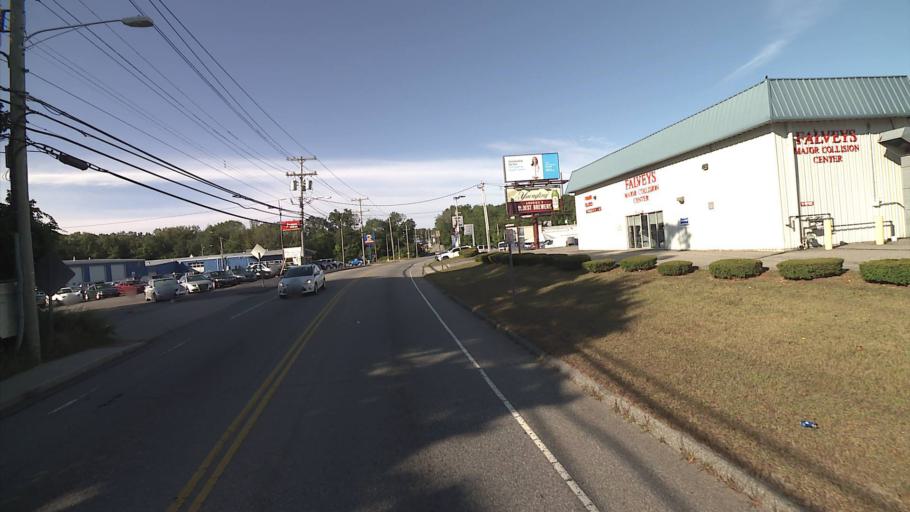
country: US
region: Connecticut
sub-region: New London County
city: Norwich
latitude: 41.5072
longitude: -72.0872
